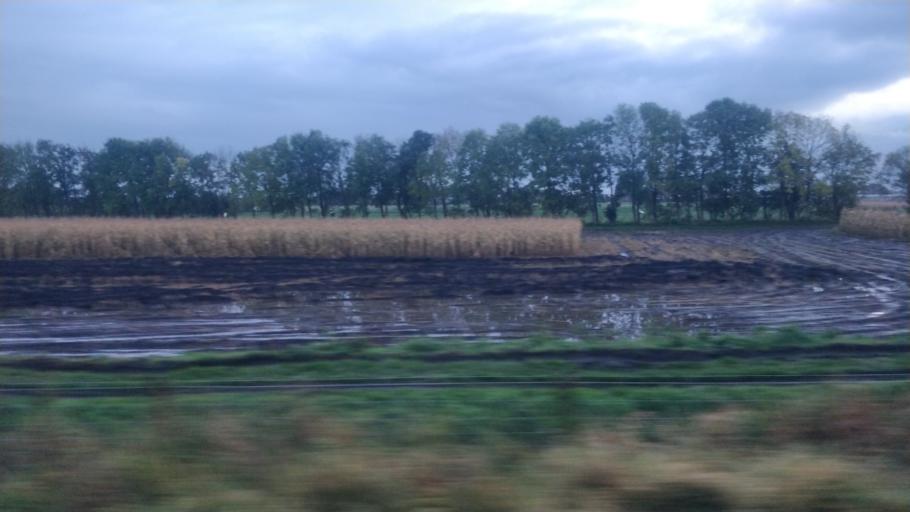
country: GB
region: England
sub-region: Lancashire
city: Ormskirk
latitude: 53.6157
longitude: -2.8828
